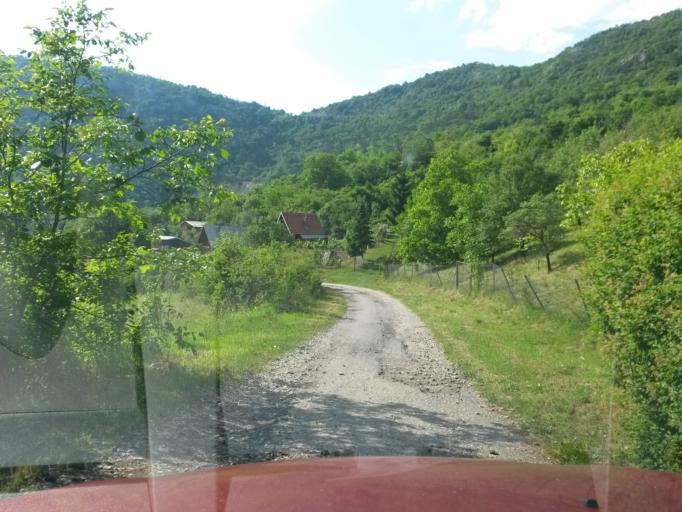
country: SK
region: Kosicky
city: Roznava
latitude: 48.5971
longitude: 20.6499
